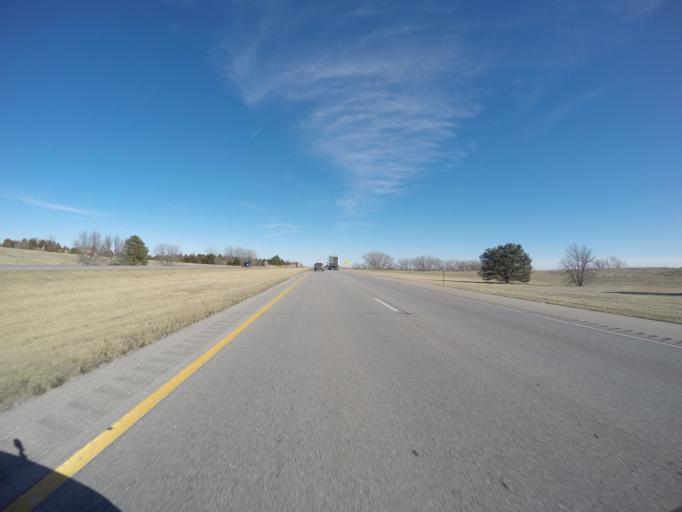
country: US
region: Nebraska
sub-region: Seward County
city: Milford
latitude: 40.8211
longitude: -96.9285
